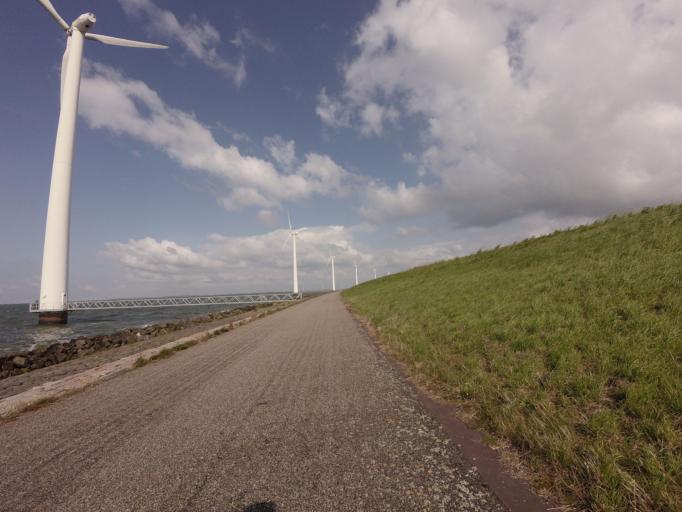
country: NL
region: Flevoland
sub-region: Gemeente Urk
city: Urk
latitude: 52.5923
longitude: 5.5593
